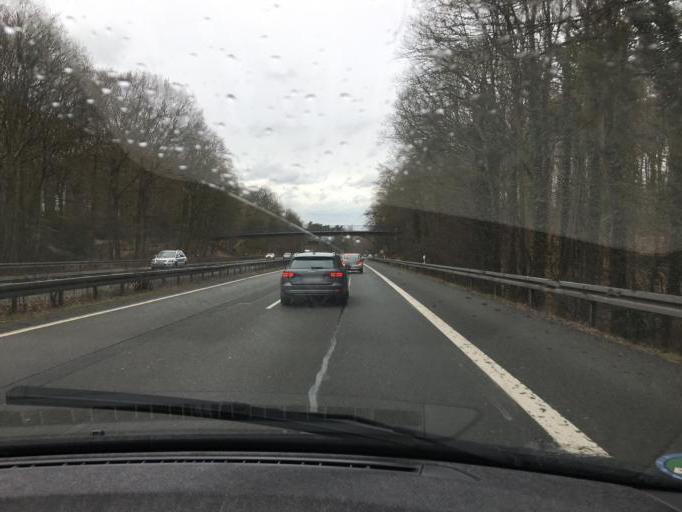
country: DE
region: North Rhine-Westphalia
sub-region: Regierungsbezirk Arnsberg
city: Dortmund
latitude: 51.4513
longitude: 7.4855
